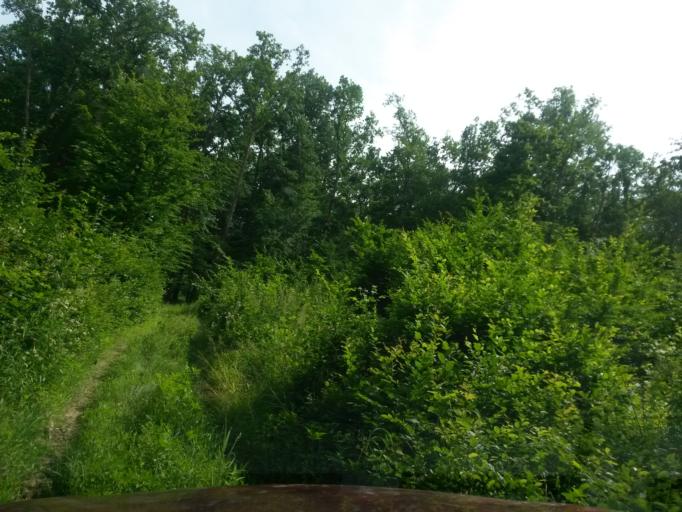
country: SK
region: Kosicky
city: Moldava nad Bodvou
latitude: 48.6424
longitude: 21.1016
